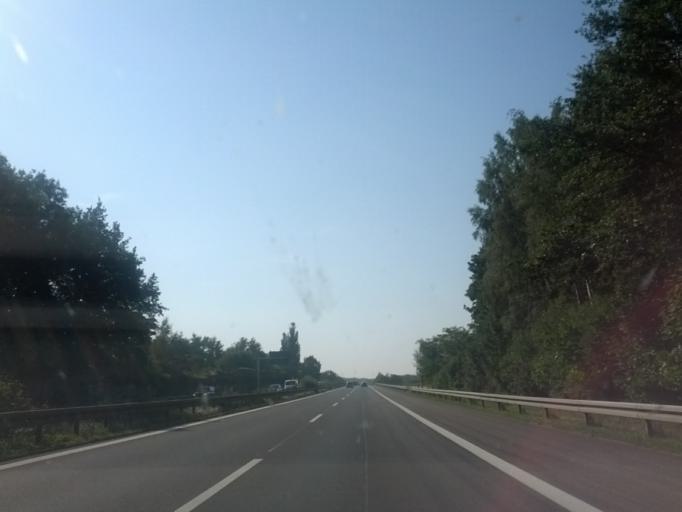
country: DE
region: Brandenburg
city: Bernau bei Berlin
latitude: 52.6819
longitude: 13.5628
